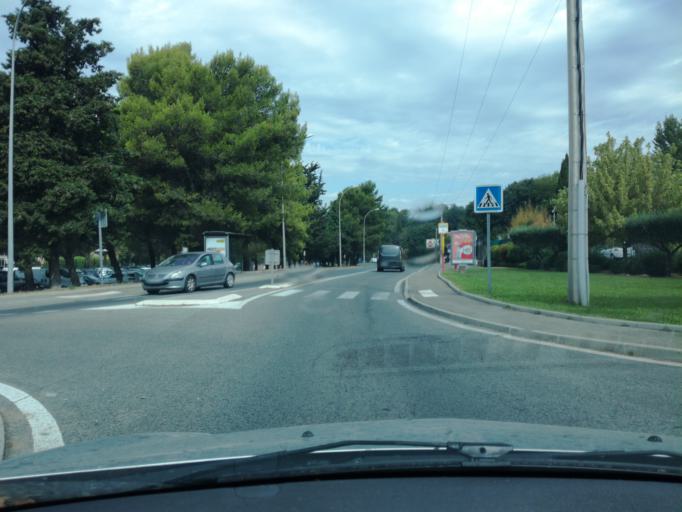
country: FR
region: Provence-Alpes-Cote d'Azur
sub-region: Departement du Var
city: Draguignan
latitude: 43.5251
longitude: 6.4605
